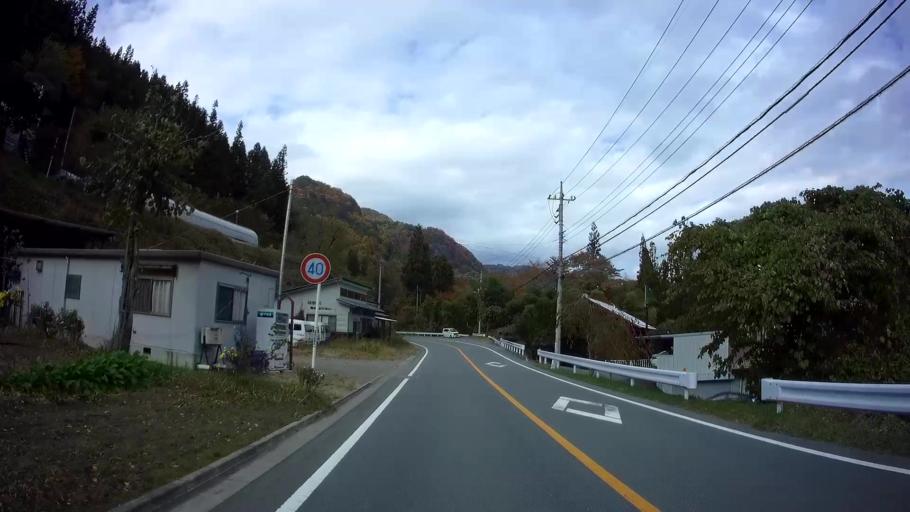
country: JP
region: Gunma
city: Nakanojomachi
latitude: 36.5896
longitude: 138.6261
